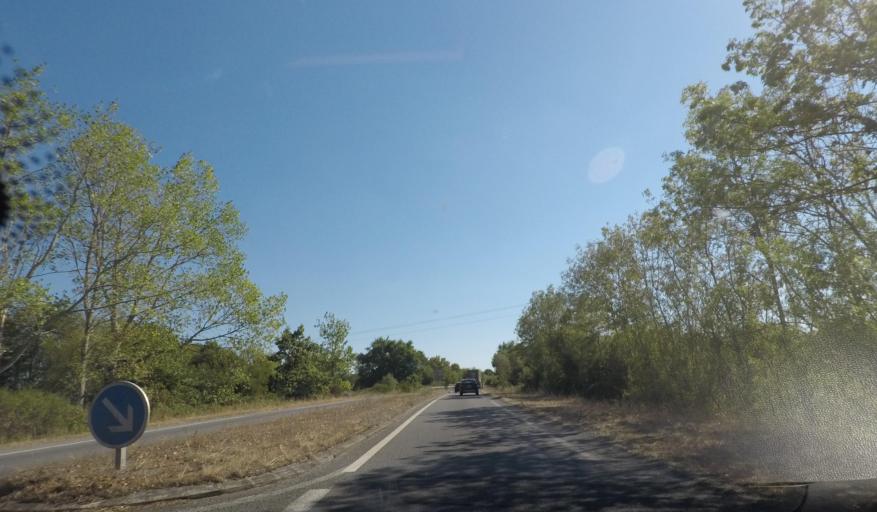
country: FR
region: Pays de la Loire
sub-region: Departement de la Loire-Atlantique
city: Besne
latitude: 47.4116
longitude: -2.0908
